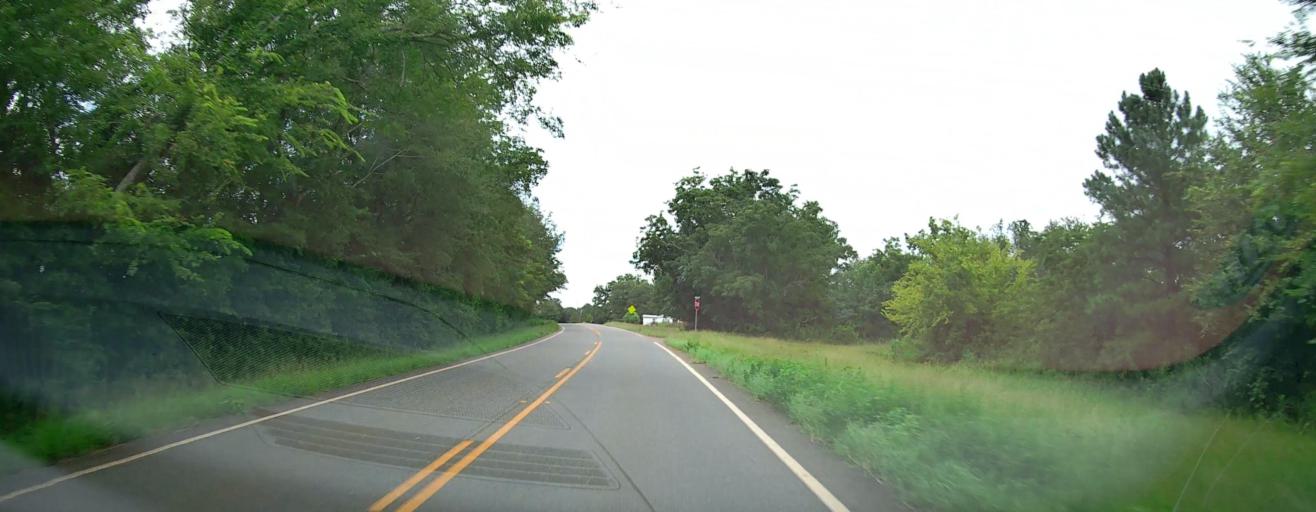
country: US
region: Georgia
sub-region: Schley County
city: Ellaville
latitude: 32.2556
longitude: -84.4059
